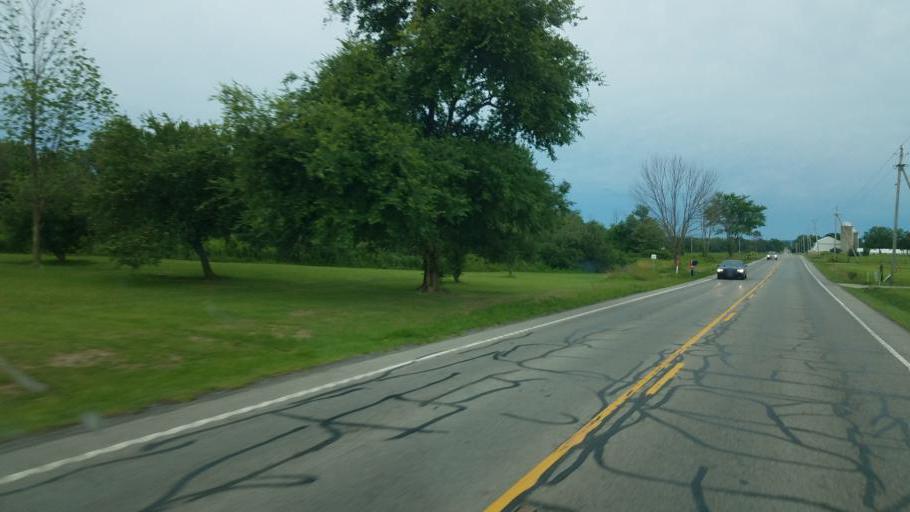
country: US
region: Ohio
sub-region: Huron County
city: Greenwich
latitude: 40.9274
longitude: -82.4970
